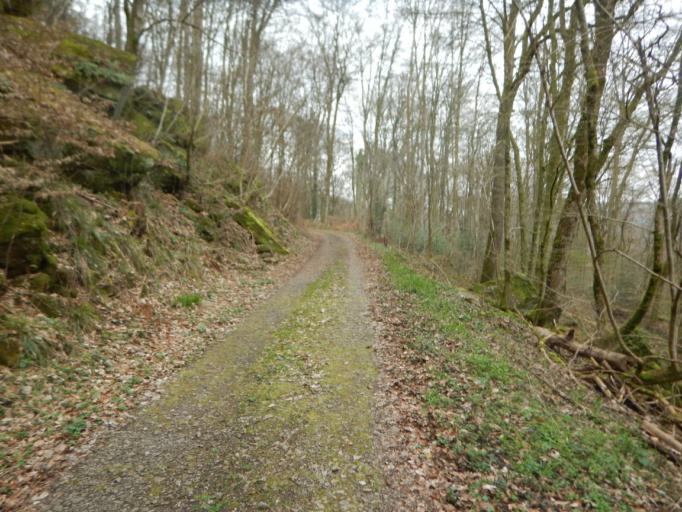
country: LU
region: Grevenmacher
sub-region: Canton d'Echternach
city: Beaufort
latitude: 49.8431
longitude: 6.3143
